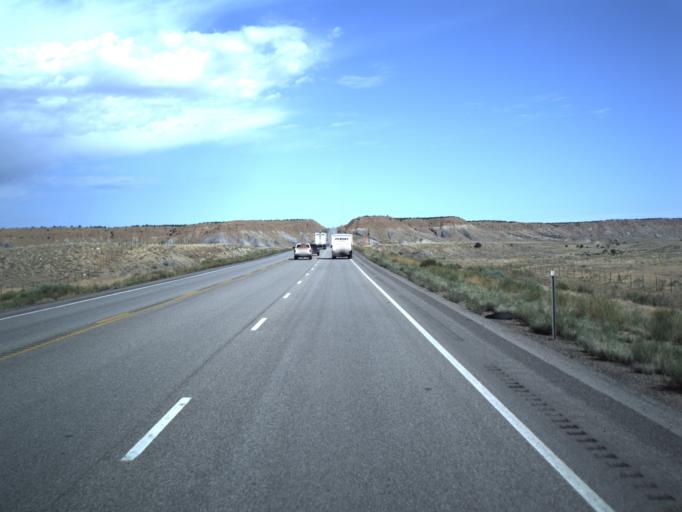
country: US
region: Utah
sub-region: Carbon County
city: East Carbon City
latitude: 39.3843
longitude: -110.4091
